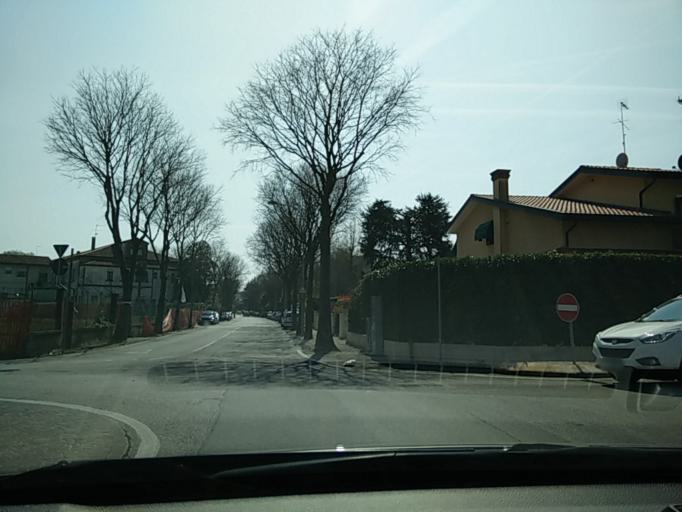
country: IT
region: Veneto
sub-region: Provincia di Venezia
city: San Dona di Piave
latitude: 45.6360
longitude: 12.5645
